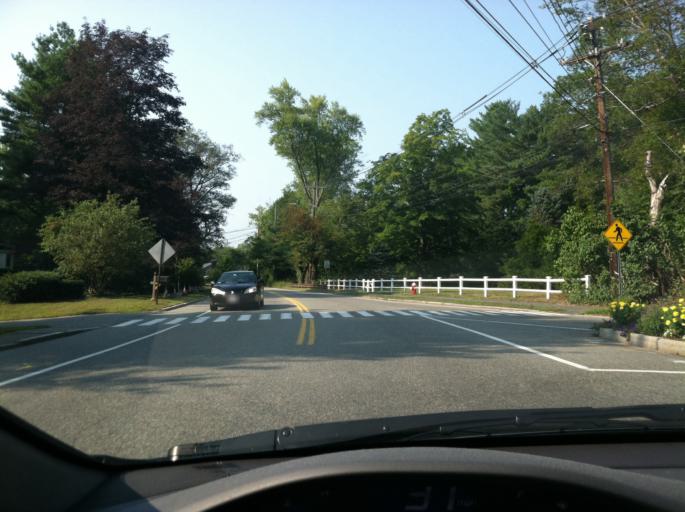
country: US
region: Massachusetts
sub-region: Middlesex County
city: Bedford
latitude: 42.5012
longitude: -71.2482
